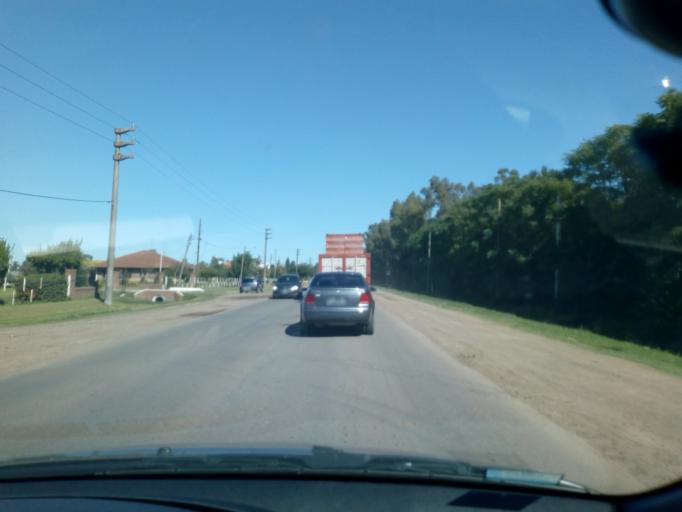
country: AR
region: Buenos Aires
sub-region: Partido de La Plata
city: La Plata
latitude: -34.9956
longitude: -58.0112
